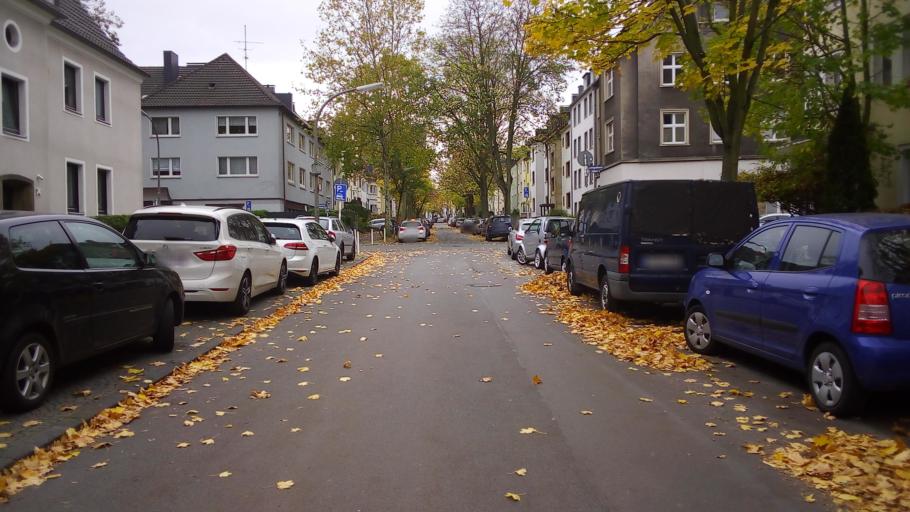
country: DE
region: North Rhine-Westphalia
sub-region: Regierungsbezirk Arnsberg
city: Dortmund
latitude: 51.5035
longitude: 7.4700
